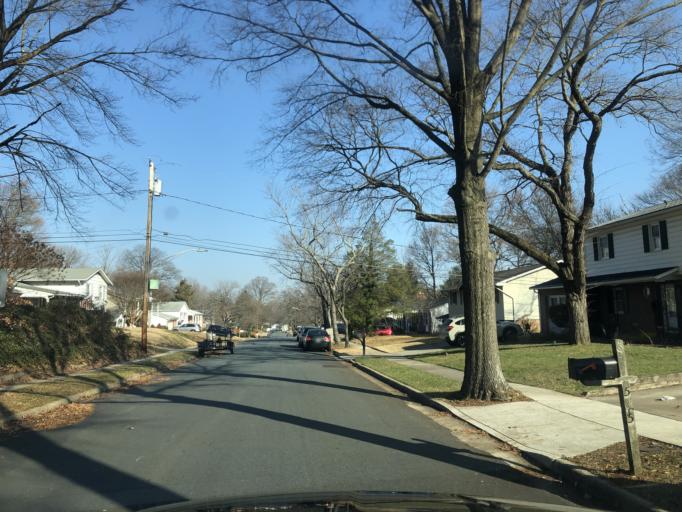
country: US
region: Maryland
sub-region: Anne Arundel County
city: Odenton
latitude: 39.0732
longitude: -76.6914
